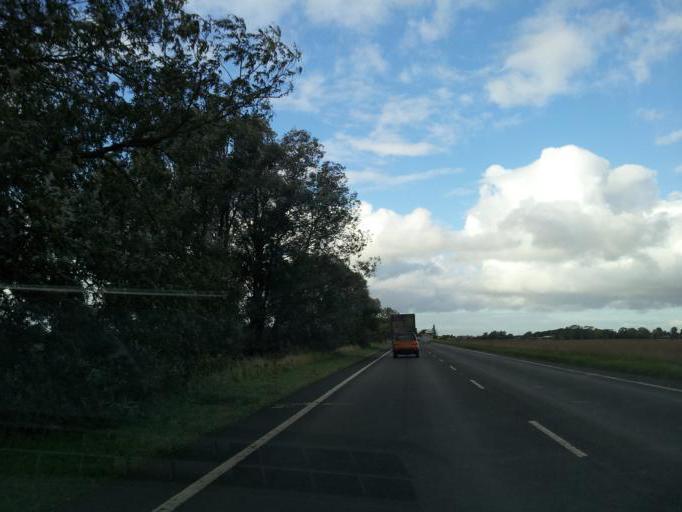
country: GB
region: England
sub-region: Norfolk
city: Terrington St Clement
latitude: 52.7467
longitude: 0.3122
